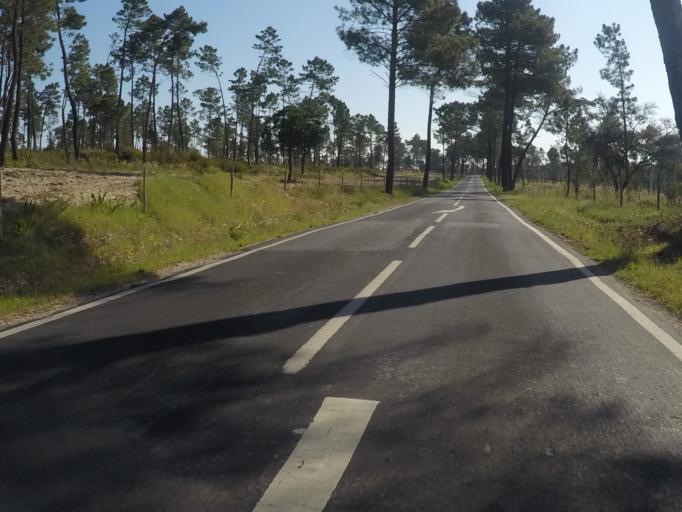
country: PT
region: Setubal
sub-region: Seixal
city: Arrentela
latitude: 38.5347
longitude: -9.1211
